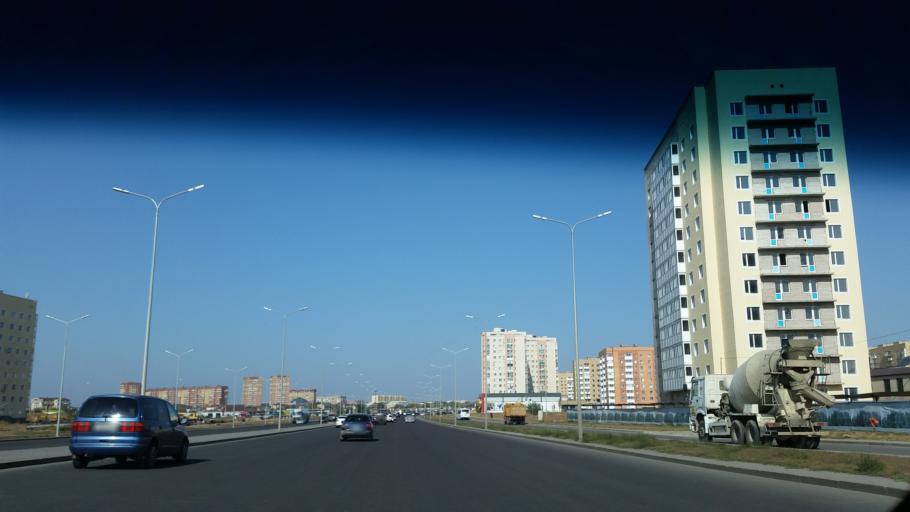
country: KZ
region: Astana Qalasy
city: Astana
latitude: 51.1678
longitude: 71.3759
